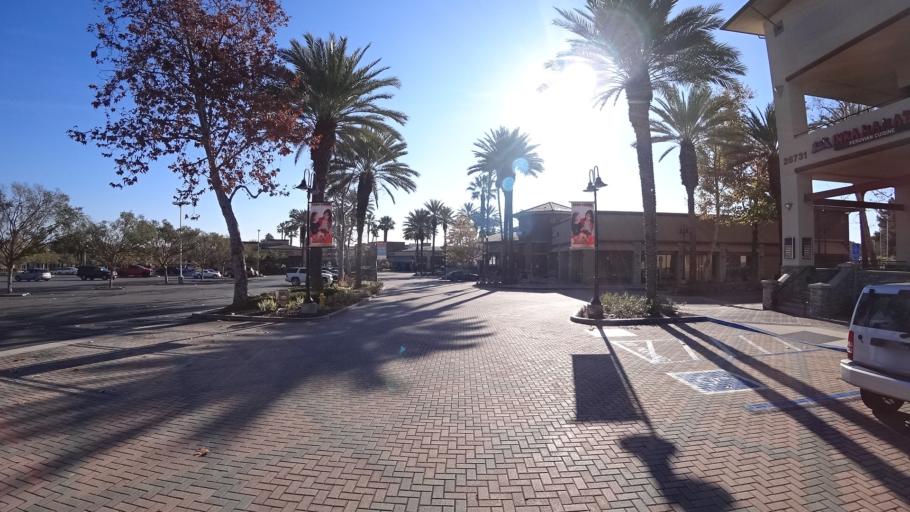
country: US
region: California
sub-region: Orange County
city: Aliso Viejo
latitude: 33.5756
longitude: -117.7261
